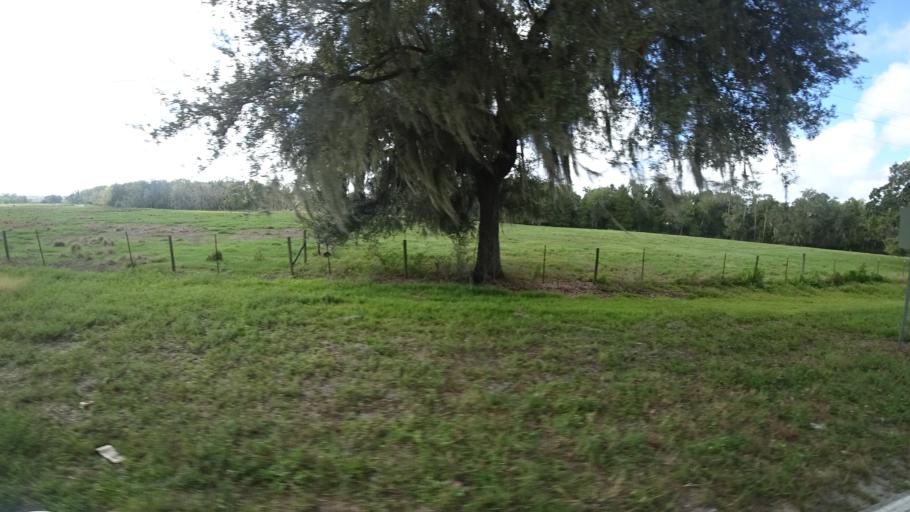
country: US
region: Florida
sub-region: Sarasota County
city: Lake Sarasota
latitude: 27.3465
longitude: -82.2424
